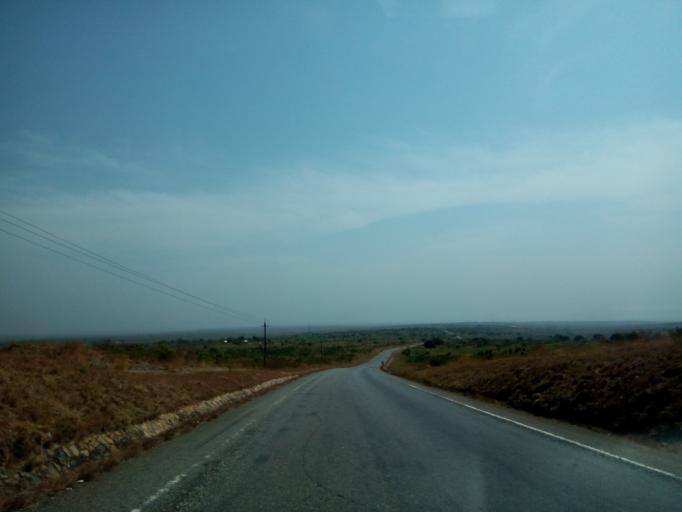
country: UG
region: Northern Region
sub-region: Nebbi District
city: Nebbi
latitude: 2.4625
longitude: 31.2943
